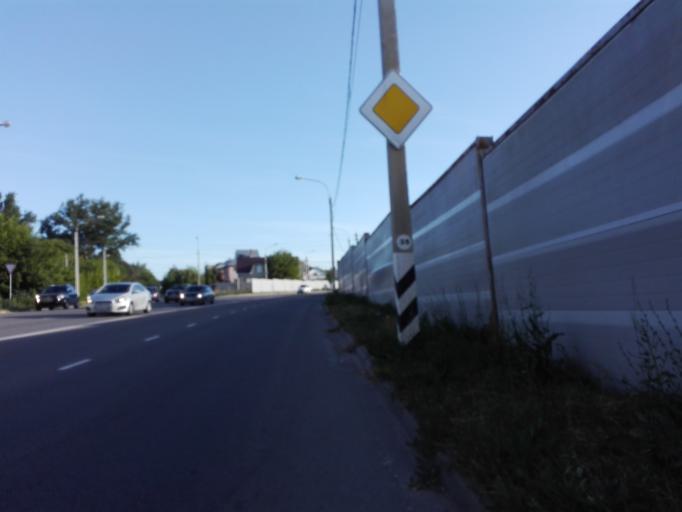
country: RU
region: Orjol
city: Orel
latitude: 52.9520
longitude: 36.0283
